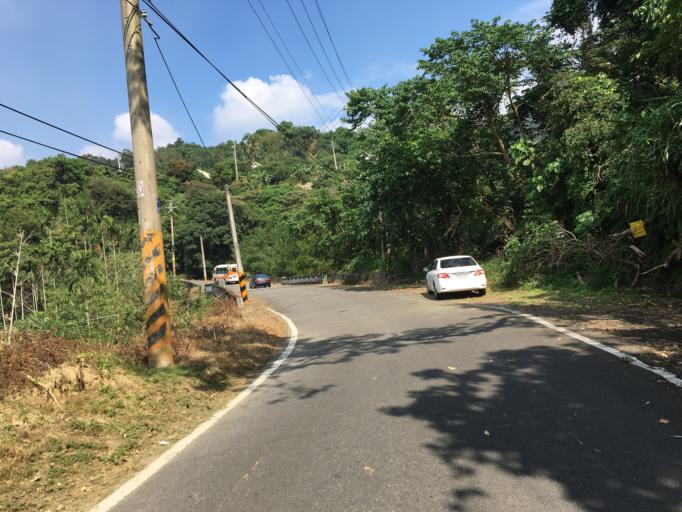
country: TW
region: Taiwan
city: Fengyuan
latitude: 24.1777
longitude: 120.7832
